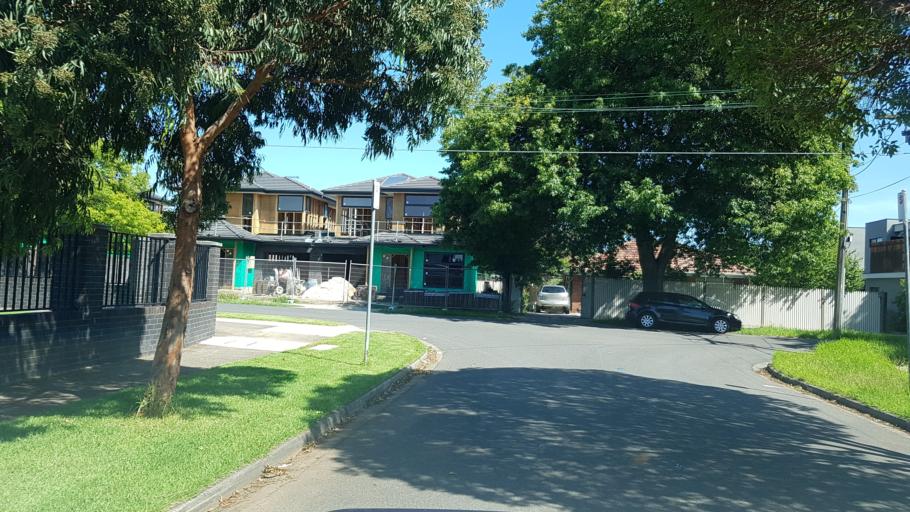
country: AU
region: Victoria
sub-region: Banyule
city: Heidelberg Heights
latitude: -37.7435
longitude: 145.0508
